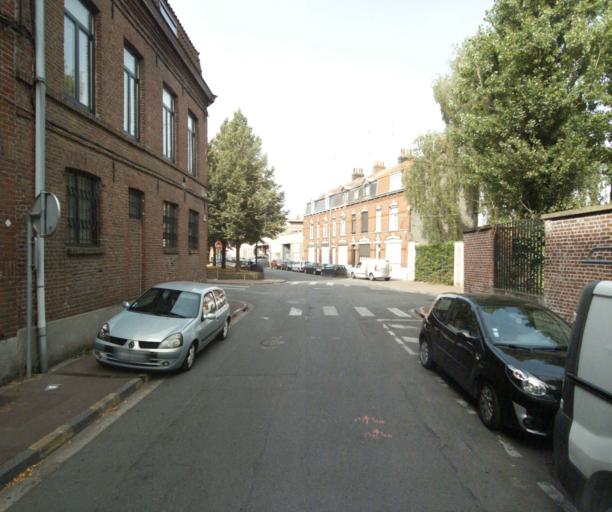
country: FR
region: Nord-Pas-de-Calais
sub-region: Departement du Nord
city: Roubaix
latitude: 50.6966
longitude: 3.1712
